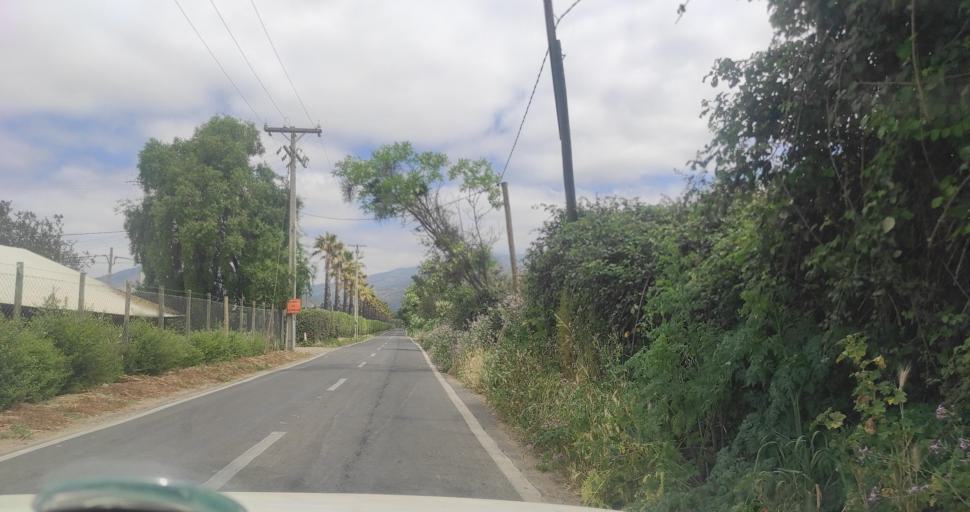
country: CL
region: Valparaiso
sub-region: Provincia de Marga Marga
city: Limache
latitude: -33.0273
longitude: -71.2291
